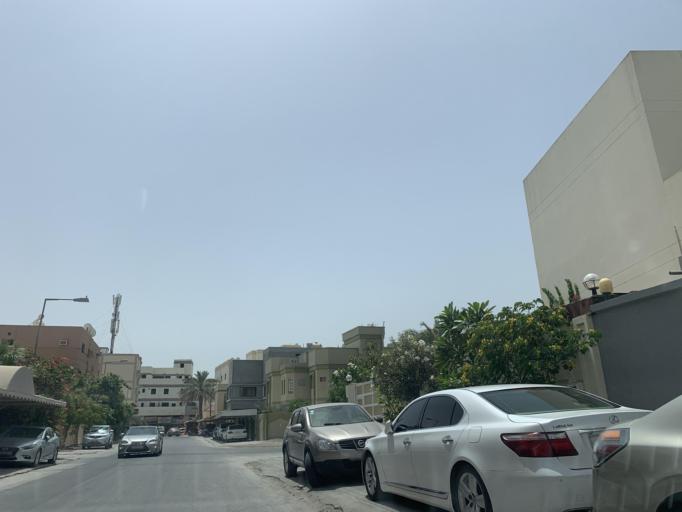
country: BH
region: Northern
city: Ar Rifa'
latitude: 26.1524
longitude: 50.5834
